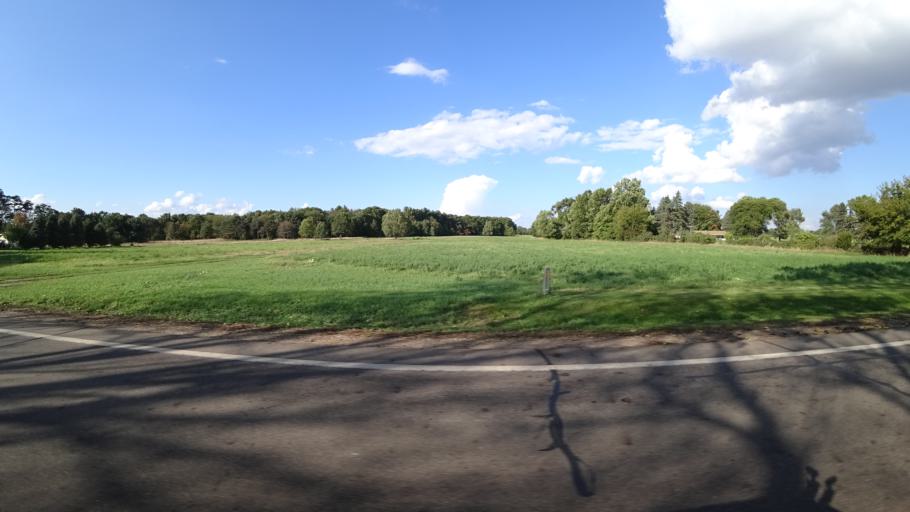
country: US
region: Michigan
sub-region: Saint Joseph County
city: Three Rivers
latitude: 41.9258
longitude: -85.5853
